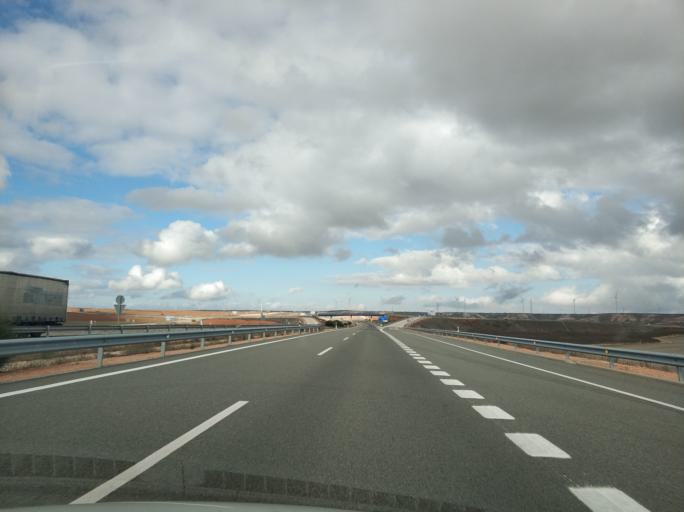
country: ES
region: Castille and Leon
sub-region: Provincia de Soria
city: Alcubilla de las Penas
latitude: 41.2564
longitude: -2.4735
